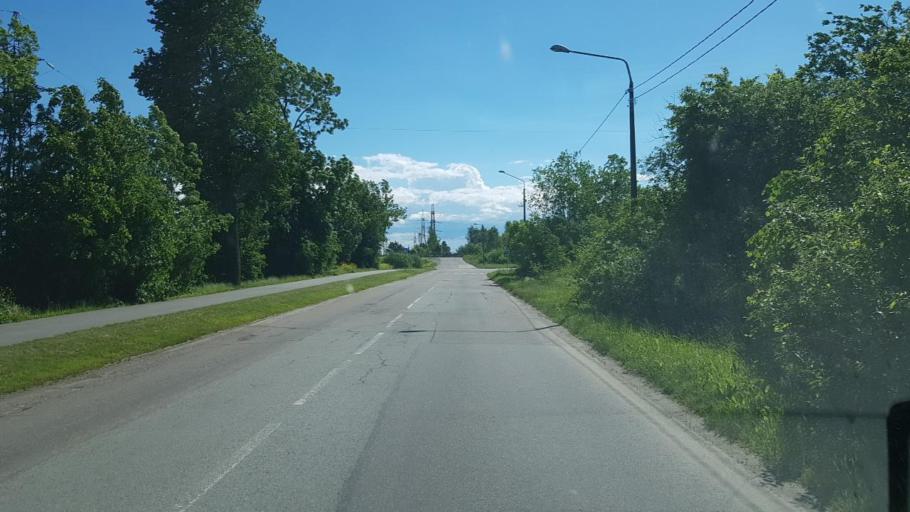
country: EE
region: Ida-Virumaa
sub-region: Narva linn
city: Narva
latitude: 59.3543
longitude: 28.1817
